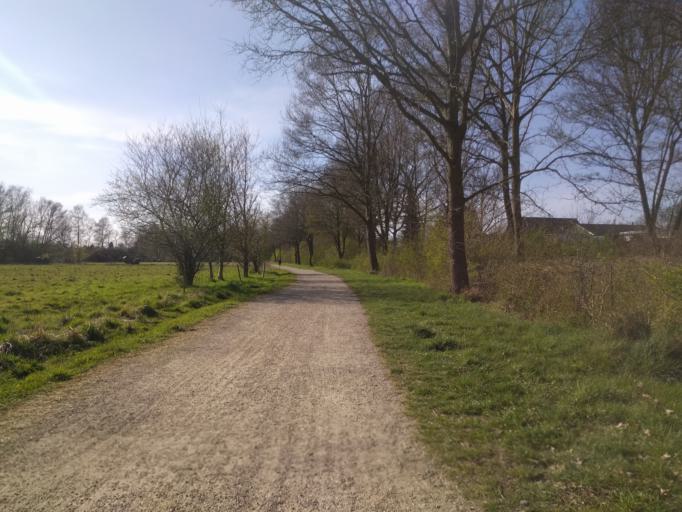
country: DK
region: South Denmark
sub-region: Odense Kommune
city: Seden
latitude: 55.3984
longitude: 10.4486
